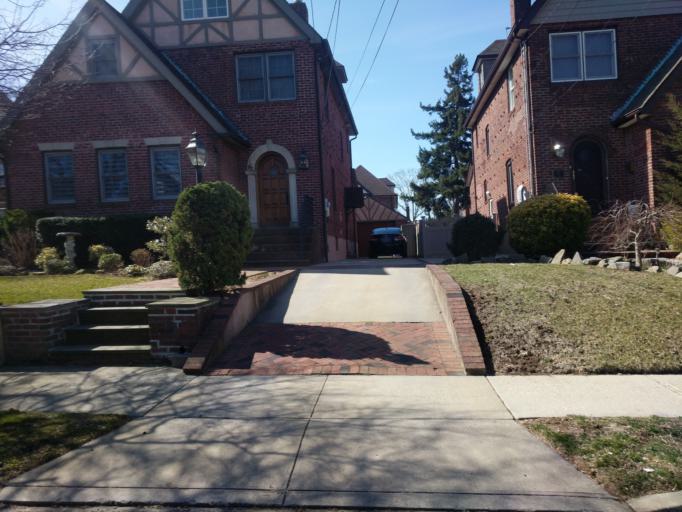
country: US
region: New York
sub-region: Nassau County
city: Lynbrook
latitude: 40.6555
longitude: -73.6865
